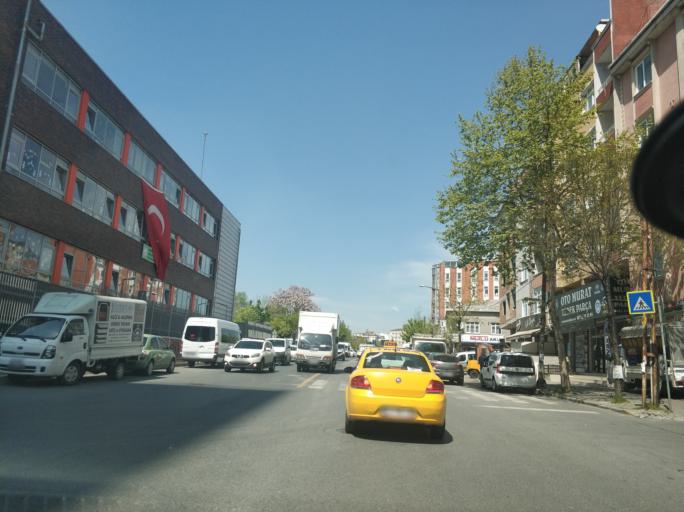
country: TR
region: Istanbul
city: Bagcilar
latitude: 41.0527
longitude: 28.8575
